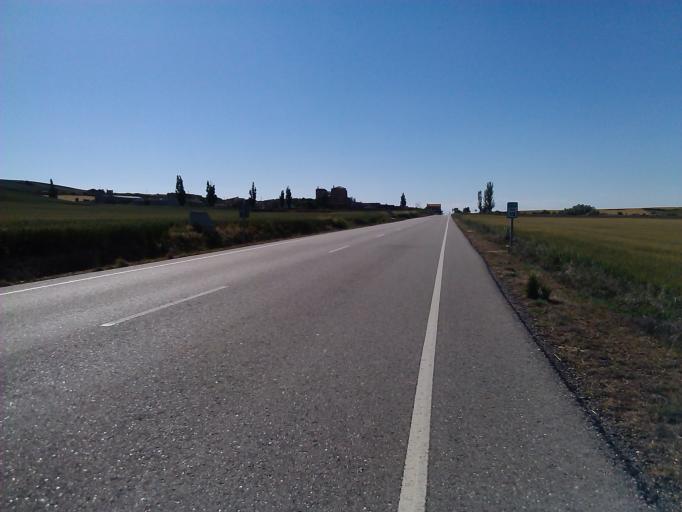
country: ES
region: Castille and Leon
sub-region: Provincia de Burgos
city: Pedrosa del Principe
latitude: 42.3061
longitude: -4.1660
